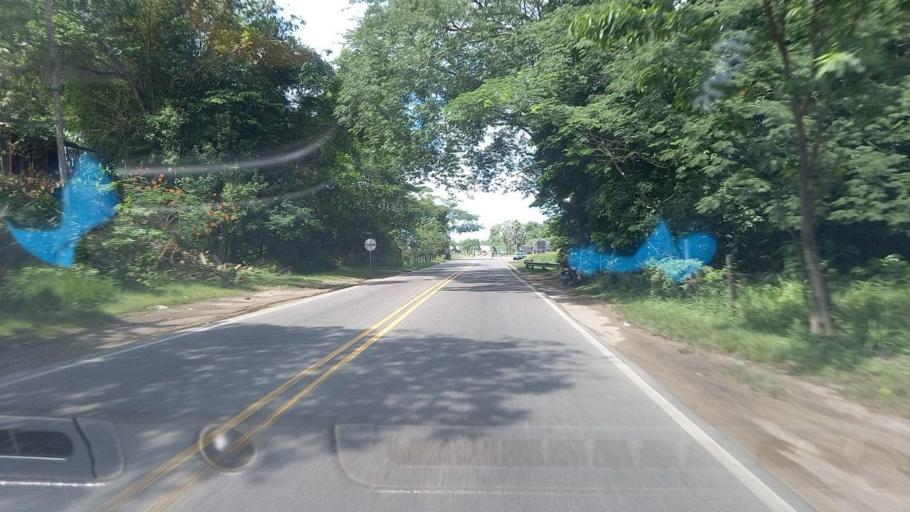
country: CO
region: Santander
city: Barrancabermeja
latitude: 7.1241
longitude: -73.5855
